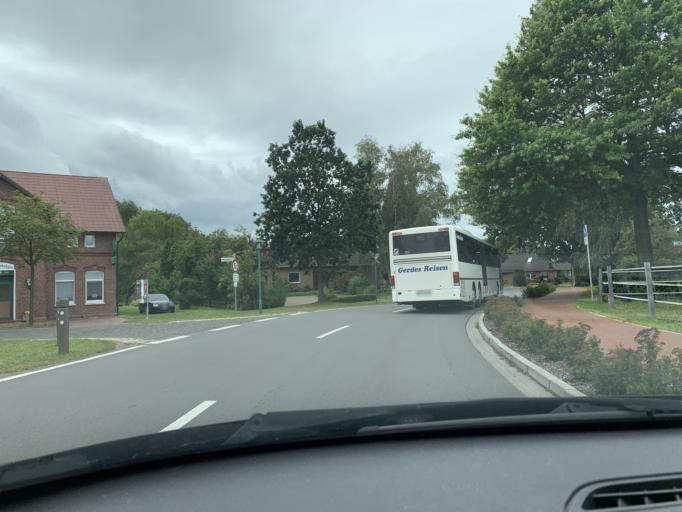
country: DE
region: Lower Saxony
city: Westerstede
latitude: 53.3162
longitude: 7.9200
